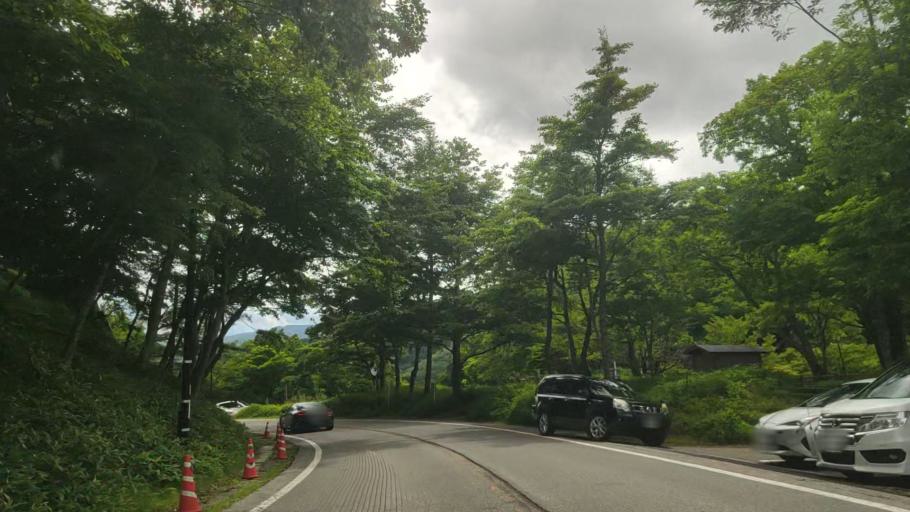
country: JP
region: Tochigi
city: Nikko
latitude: 36.7966
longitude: 139.4289
